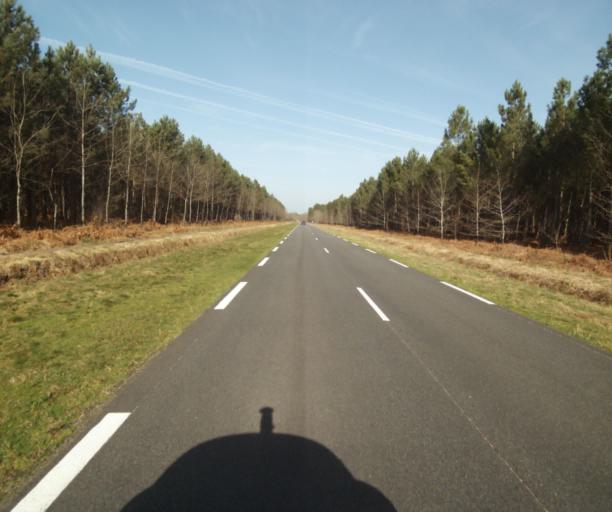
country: FR
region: Aquitaine
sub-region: Departement de la Gironde
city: Grignols
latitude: 44.1900
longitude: -0.1158
